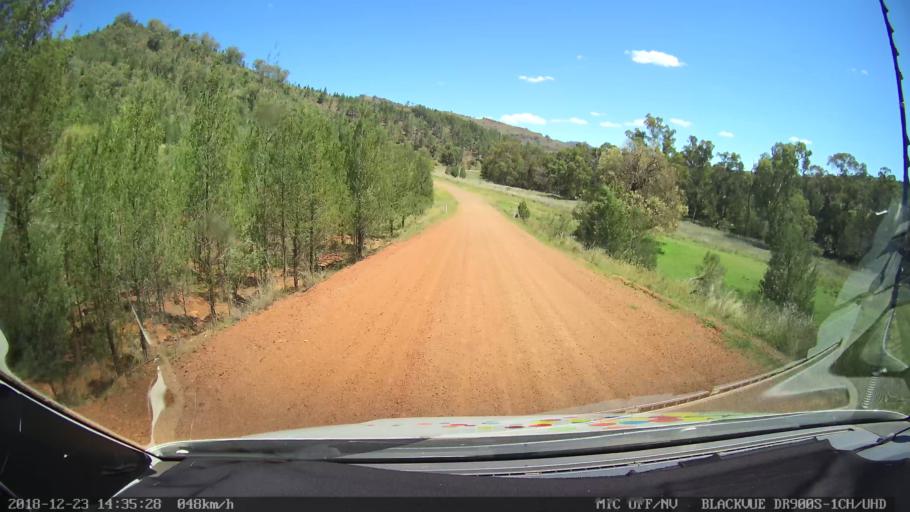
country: AU
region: New South Wales
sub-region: Tamworth Municipality
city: Manilla
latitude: -30.6104
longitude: 150.9079
